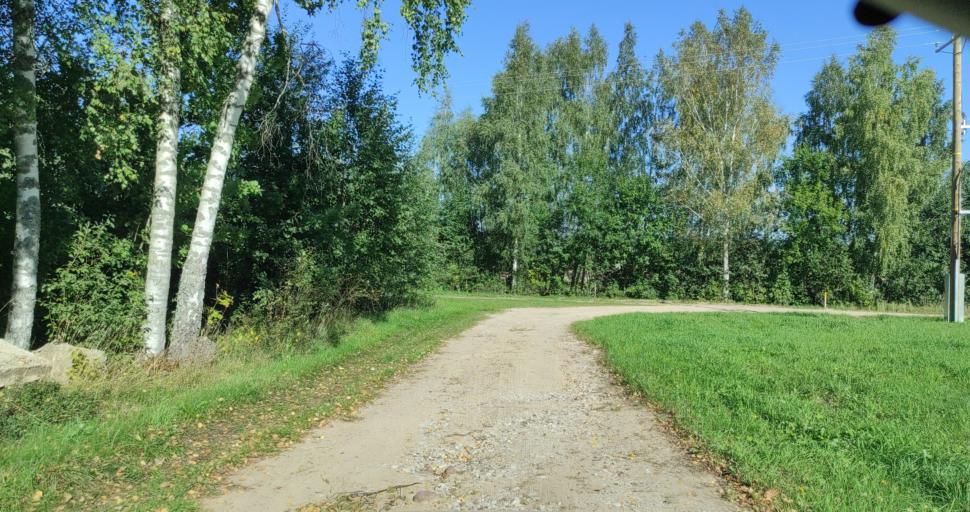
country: LV
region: Kuldigas Rajons
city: Kuldiga
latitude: 56.9739
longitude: 21.9225
